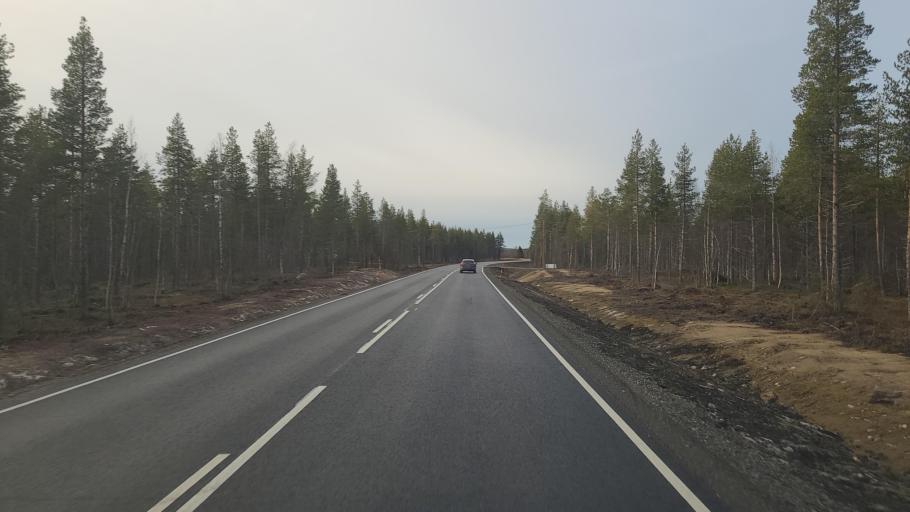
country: FI
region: Lapland
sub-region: Tunturi-Lappi
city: Kittilae
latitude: 67.8712
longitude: 24.9063
